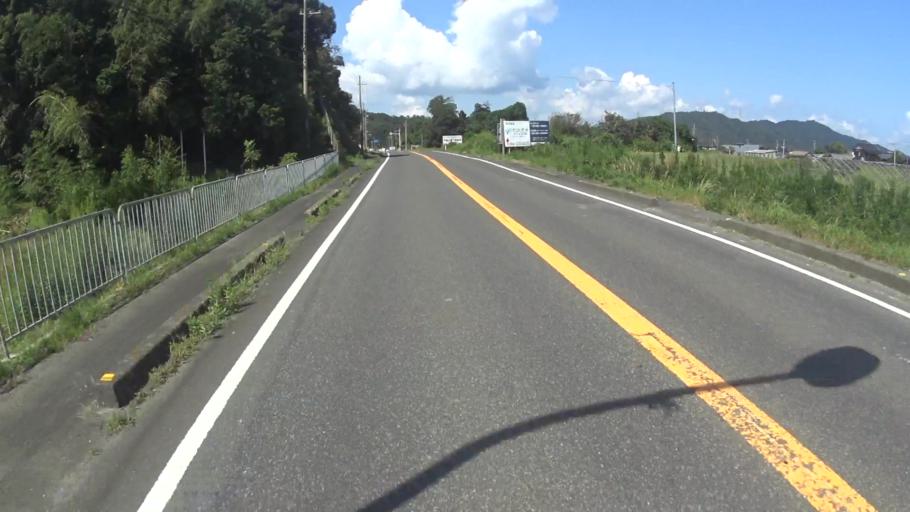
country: JP
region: Kyoto
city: Miyazu
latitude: 35.5376
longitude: 135.2384
